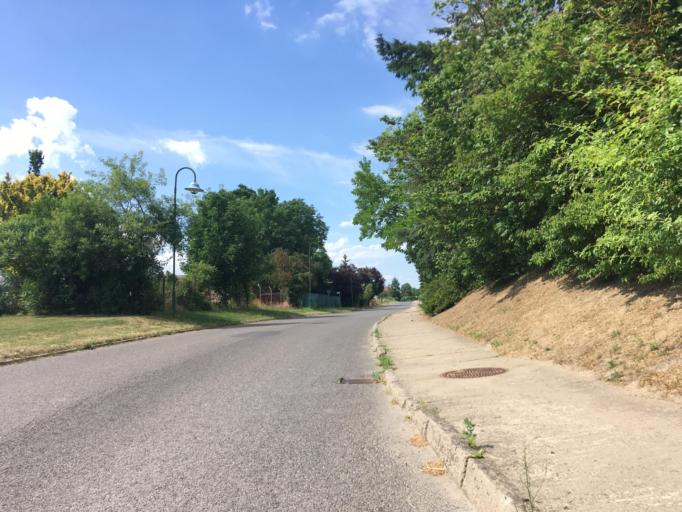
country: DE
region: Brandenburg
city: Zichow
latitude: 53.1536
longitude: 14.0328
